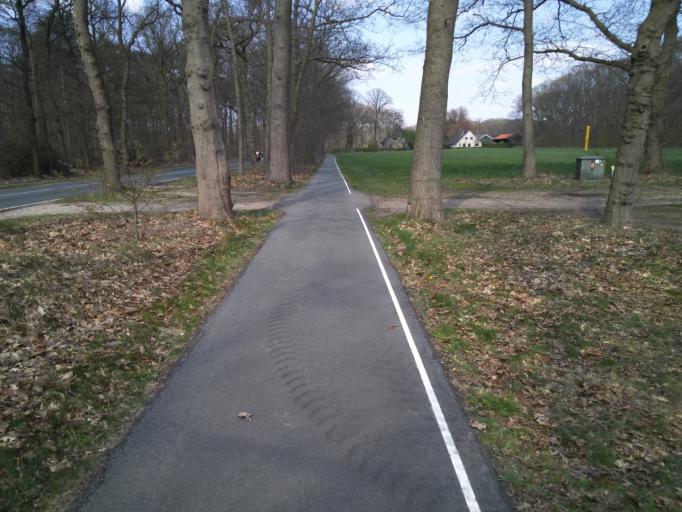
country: NL
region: Gelderland
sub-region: Gemeente Renkum
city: Wolfheze
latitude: 52.0215
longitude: 5.8242
